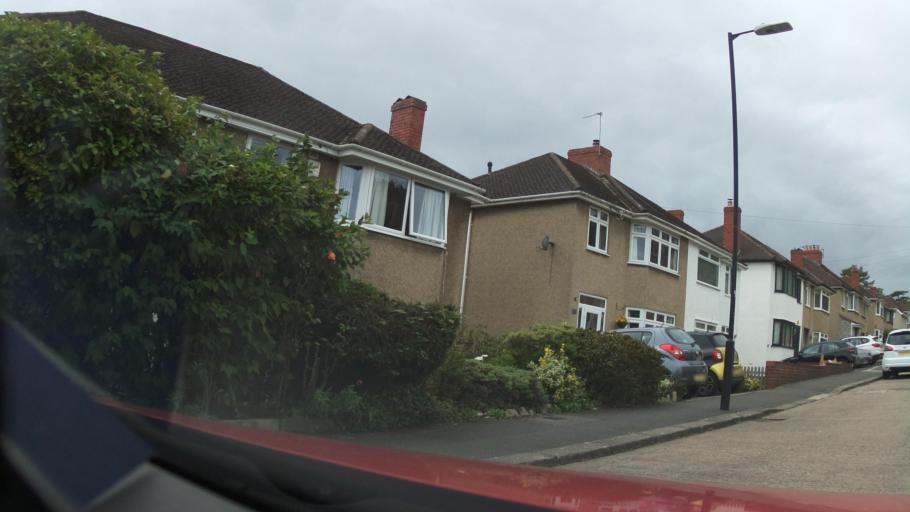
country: GB
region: England
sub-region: North Somerset
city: Easton-in-Gordano
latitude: 51.4942
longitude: -2.6494
